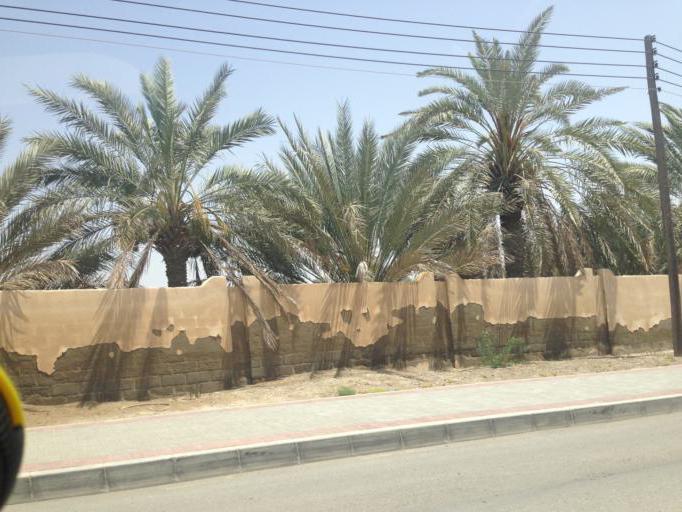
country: OM
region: Muhafazat Masqat
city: As Sib al Jadidah
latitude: 23.6939
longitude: 58.1071
